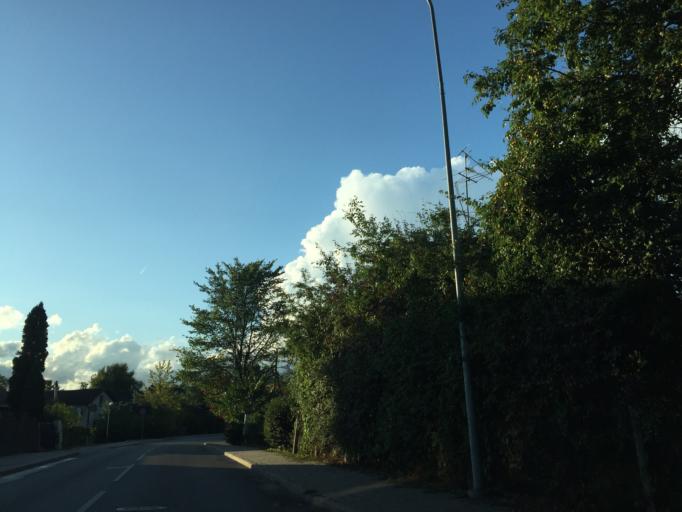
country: LV
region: Jelgava
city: Jelgava
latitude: 56.6449
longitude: 23.7165
